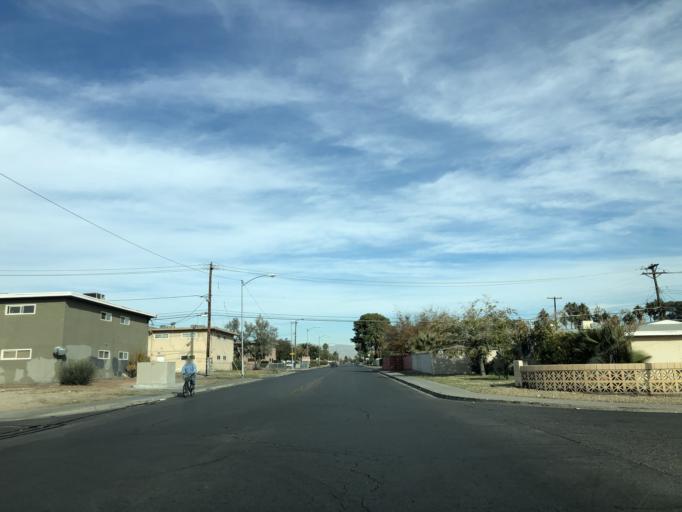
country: US
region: Nevada
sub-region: Clark County
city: Winchester
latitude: 36.1306
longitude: -115.1321
